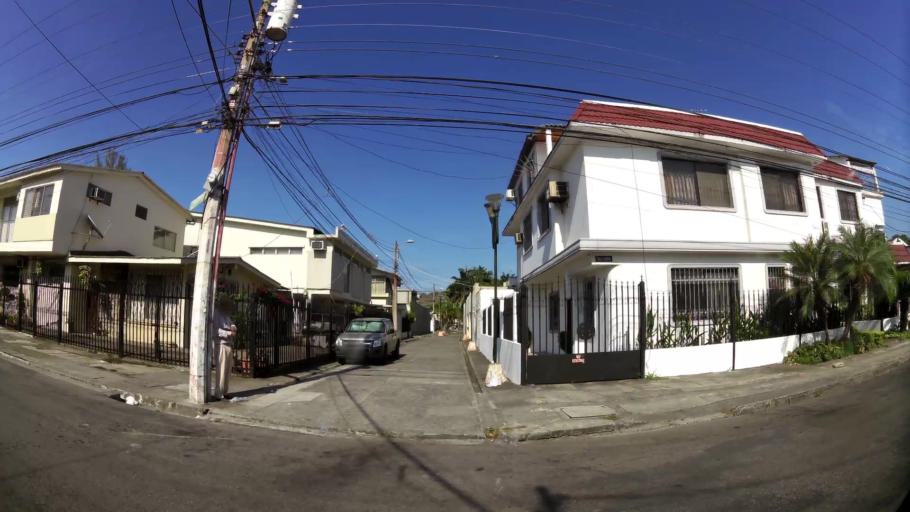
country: EC
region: Guayas
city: Guayaquil
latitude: -2.1696
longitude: -79.9076
